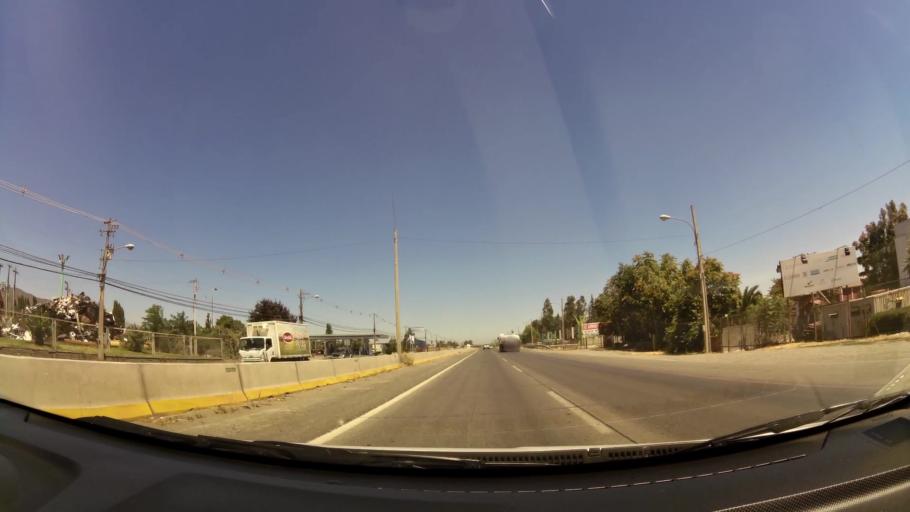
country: CL
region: O'Higgins
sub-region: Provincia de Cachapoal
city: Rancagua
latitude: -34.2060
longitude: -70.7645
